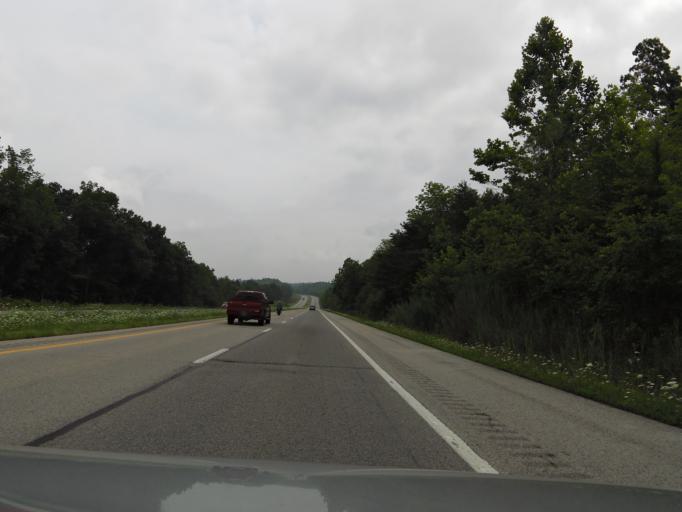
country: US
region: Kentucky
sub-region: Ohio County
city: Beaver Dam
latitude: 37.3344
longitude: -86.9561
